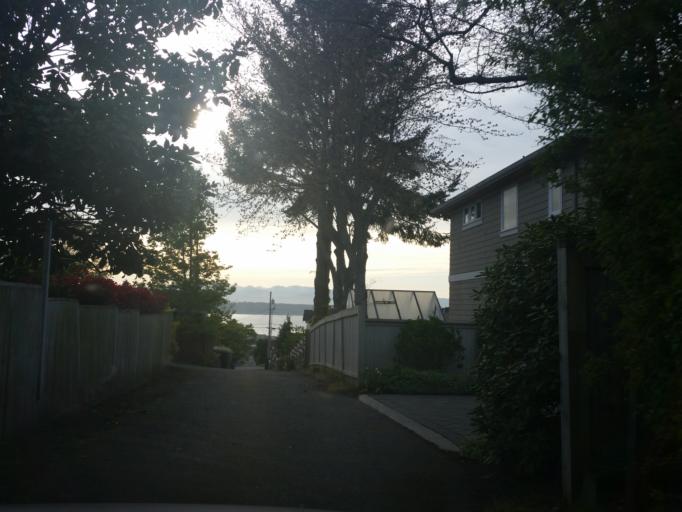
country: US
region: Washington
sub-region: Snohomish County
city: Edmonds
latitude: 47.8109
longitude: -122.3679
